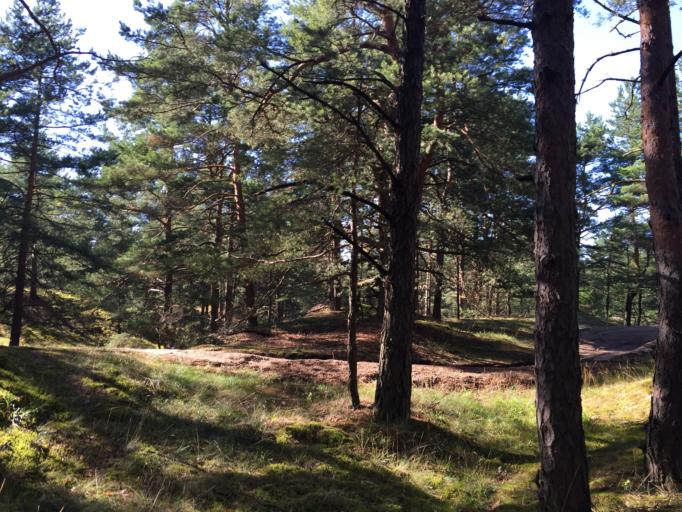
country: LV
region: Riga
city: Jaunciems
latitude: 57.0826
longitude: 24.1384
